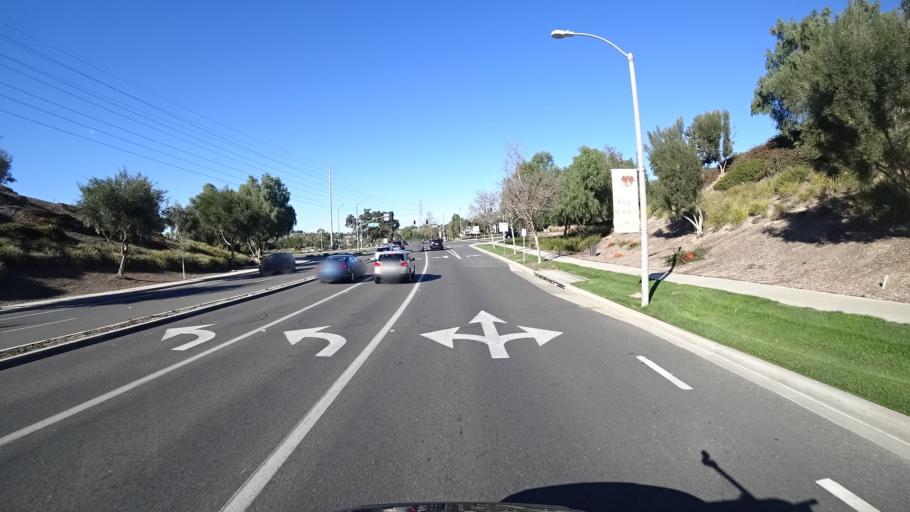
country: US
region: California
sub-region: Orange County
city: Ladera Ranch
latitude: 33.5645
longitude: -117.6432
